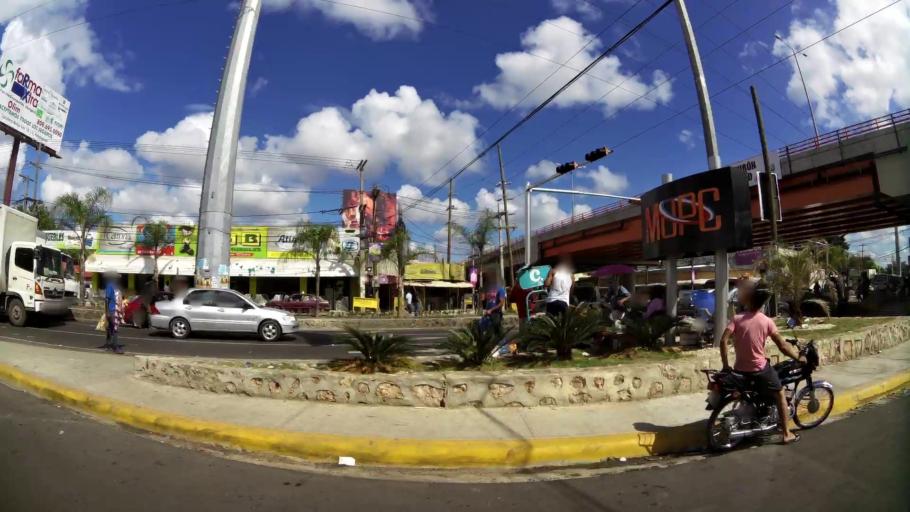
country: DO
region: Santo Domingo
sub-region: Santo Domingo
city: Santo Domingo Este
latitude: 18.5189
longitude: -69.8350
